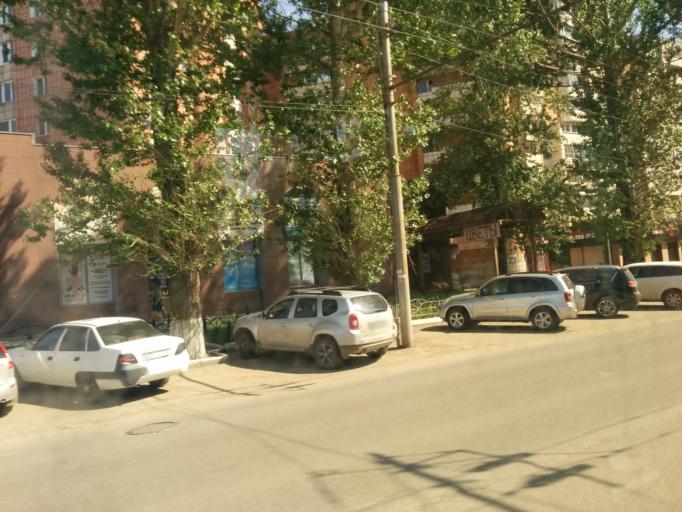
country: RU
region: Perm
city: Perm
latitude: 58.0138
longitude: 56.2810
